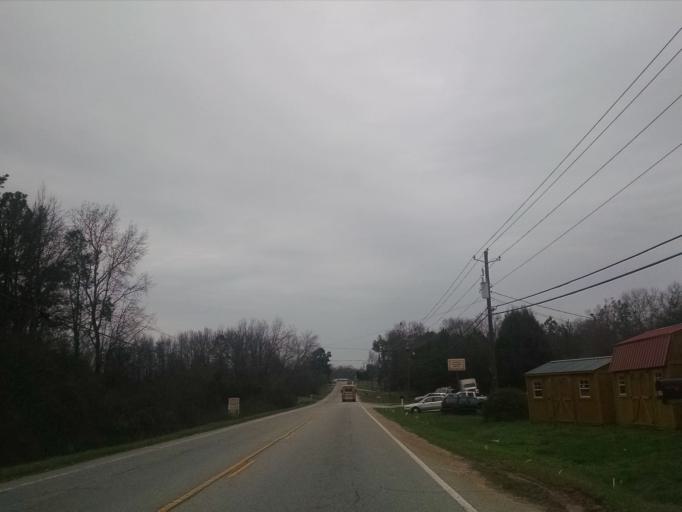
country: US
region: Georgia
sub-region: Hall County
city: Oakwood
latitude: 34.2095
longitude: -83.8821
